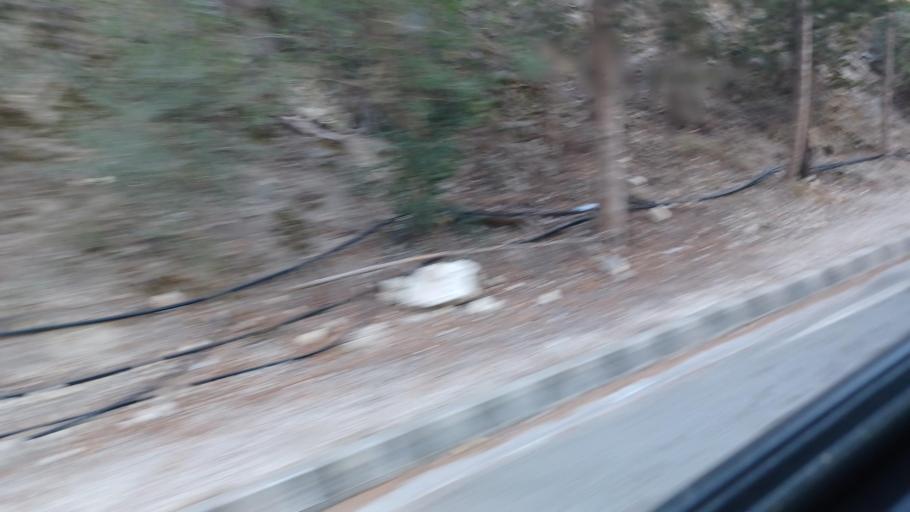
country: CY
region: Pafos
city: Tala
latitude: 34.8454
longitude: 32.4466
